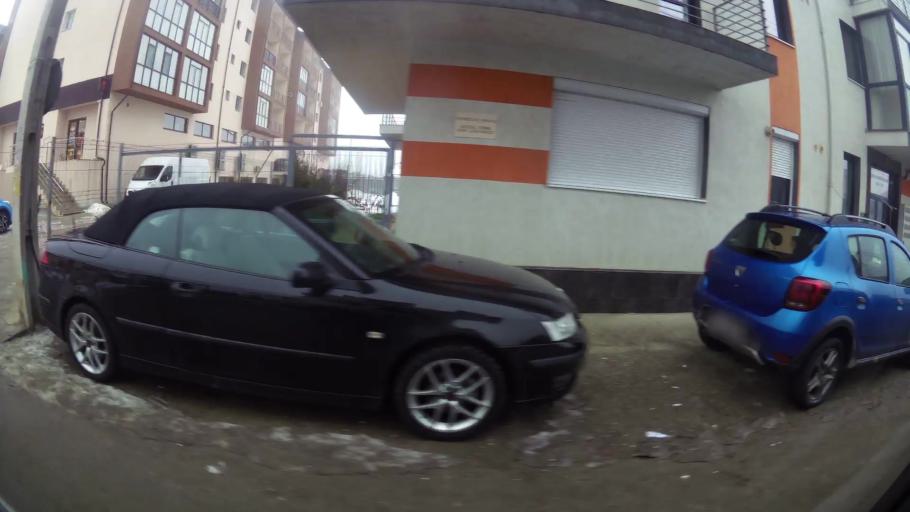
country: RO
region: Ilfov
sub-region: Comuna Chiajna
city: Rosu
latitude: 44.4446
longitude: 26.0073
